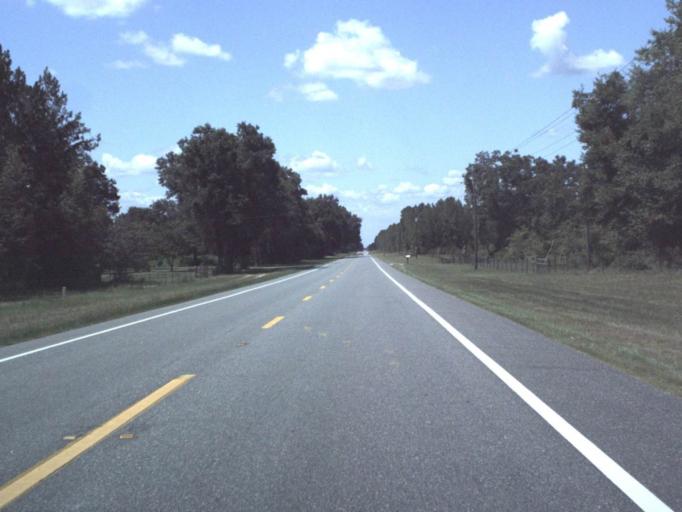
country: US
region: Florida
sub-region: Alachua County
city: High Springs
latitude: 29.7920
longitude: -82.7410
